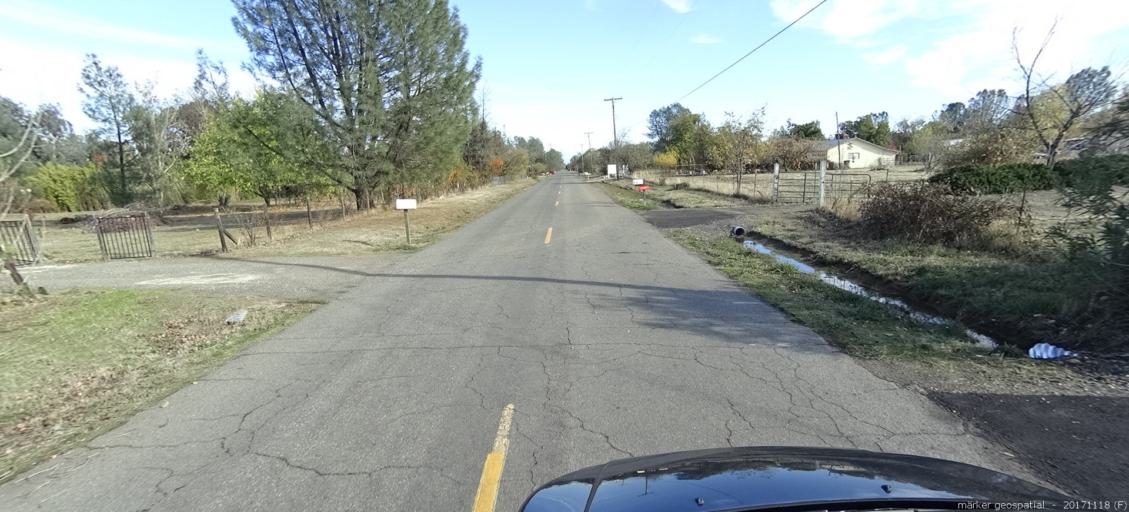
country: US
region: California
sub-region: Shasta County
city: Redding
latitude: 40.4690
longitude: -122.4193
